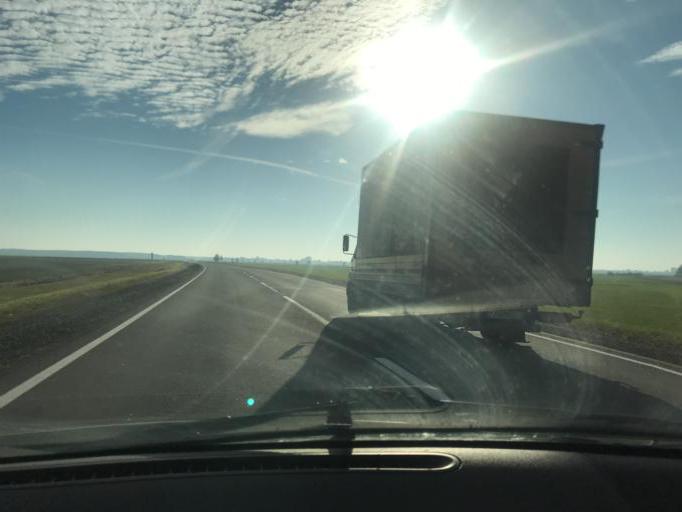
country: BY
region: Brest
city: Drahichyn
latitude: 52.1940
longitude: 25.2498
